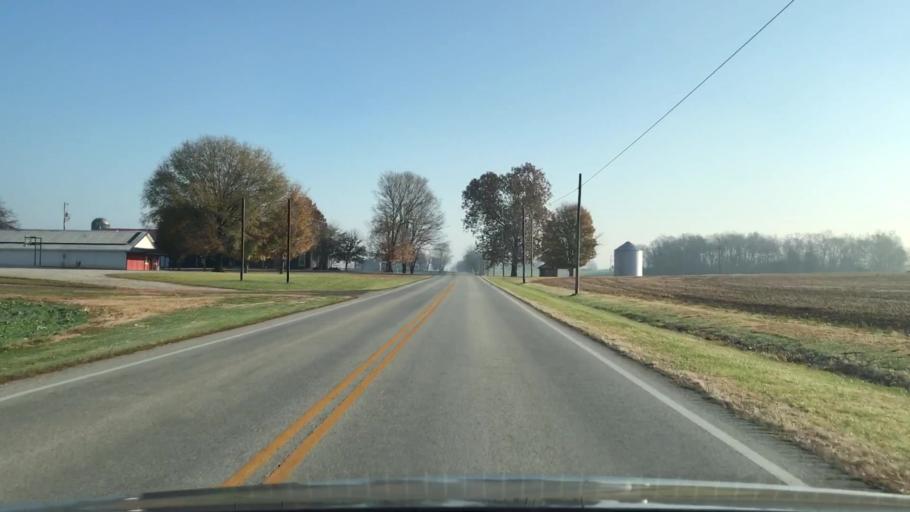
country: US
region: Kentucky
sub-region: Edmonson County
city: Brownsville
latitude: 37.0786
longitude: -86.2457
